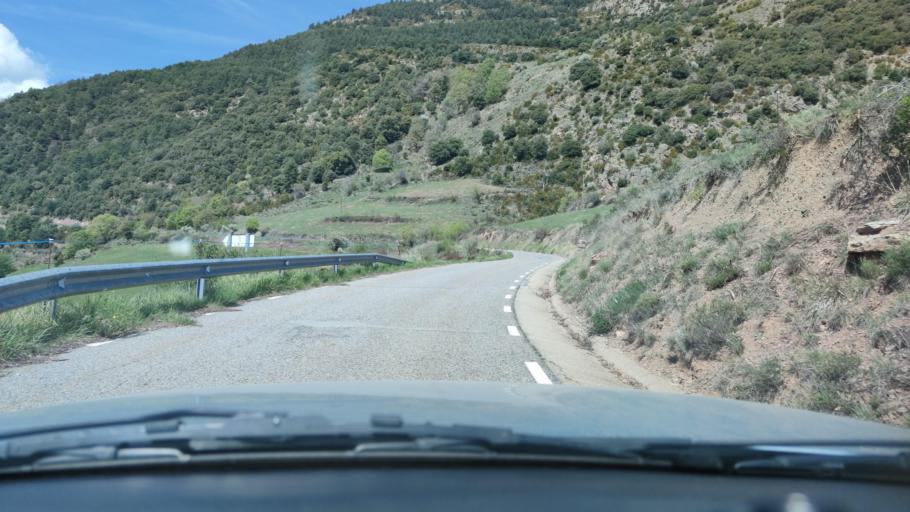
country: ES
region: Catalonia
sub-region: Provincia de Lleida
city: Coll de Nargo
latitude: 42.2973
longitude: 1.2752
